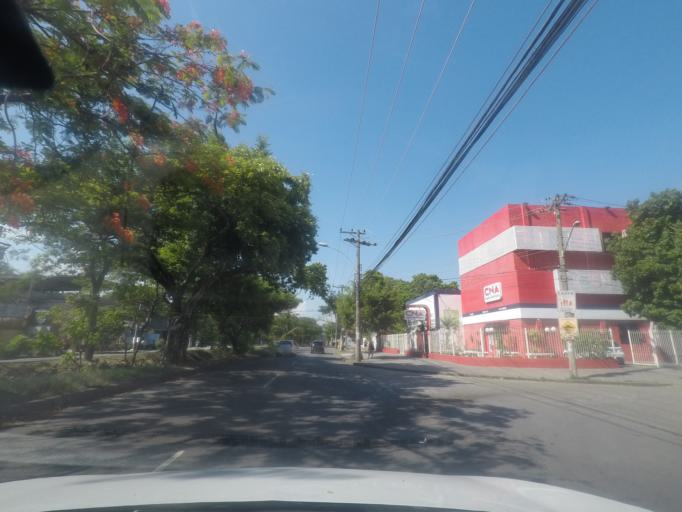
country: BR
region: Rio de Janeiro
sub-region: Sao Joao De Meriti
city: Sao Joao de Meriti
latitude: -22.8802
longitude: -43.3702
